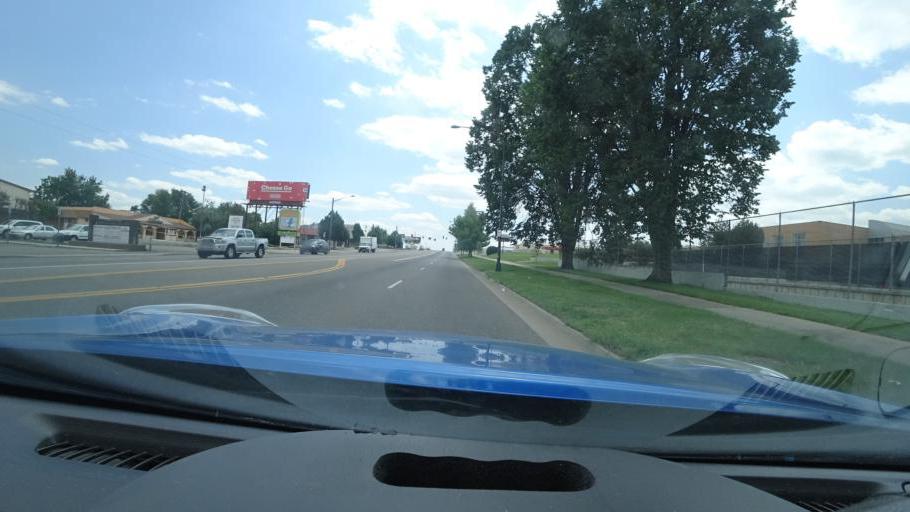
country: US
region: Colorado
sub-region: Arapahoe County
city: Sheridan
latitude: 39.6767
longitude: -105.0251
